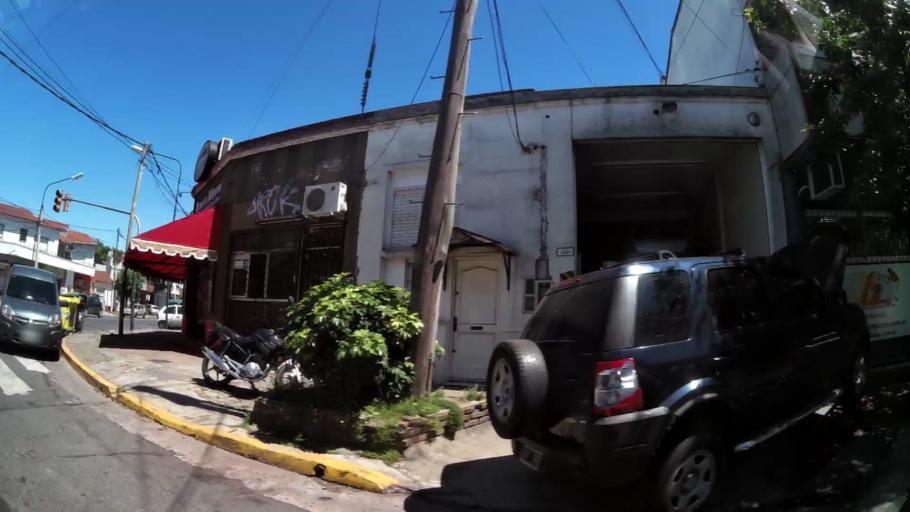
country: AR
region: Buenos Aires
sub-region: Partido de San Isidro
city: San Isidro
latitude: -34.4744
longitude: -58.5314
